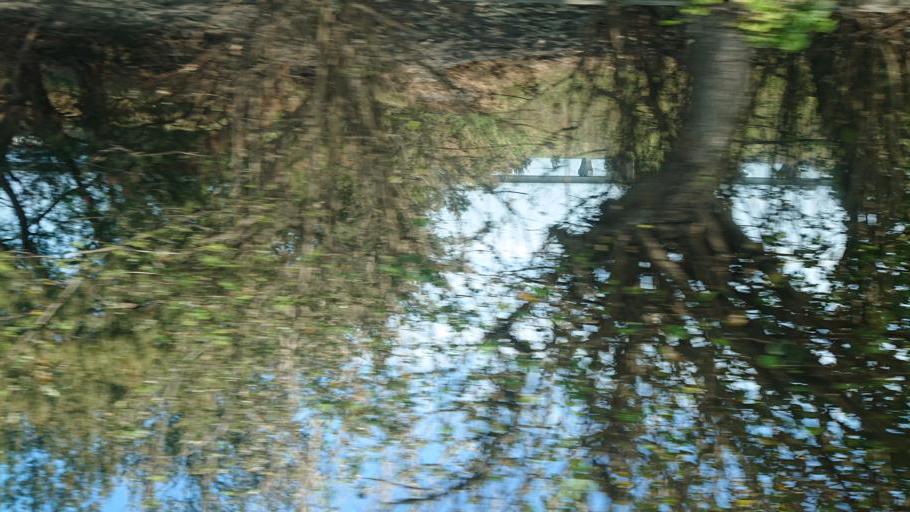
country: TW
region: Taiwan
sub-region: Changhua
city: Chang-hua
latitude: 23.9108
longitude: 120.3102
